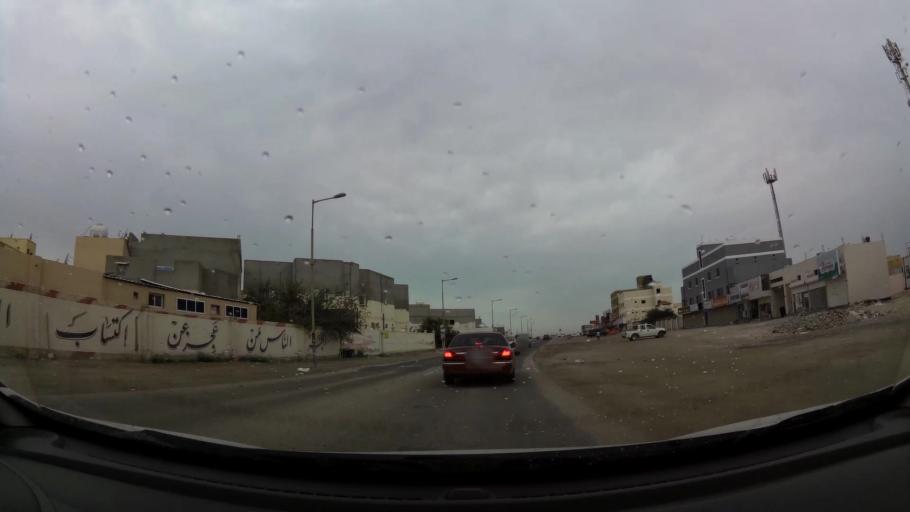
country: BH
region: Central Governorate
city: Madinat Hamad
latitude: 26.1281
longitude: 50.4777
